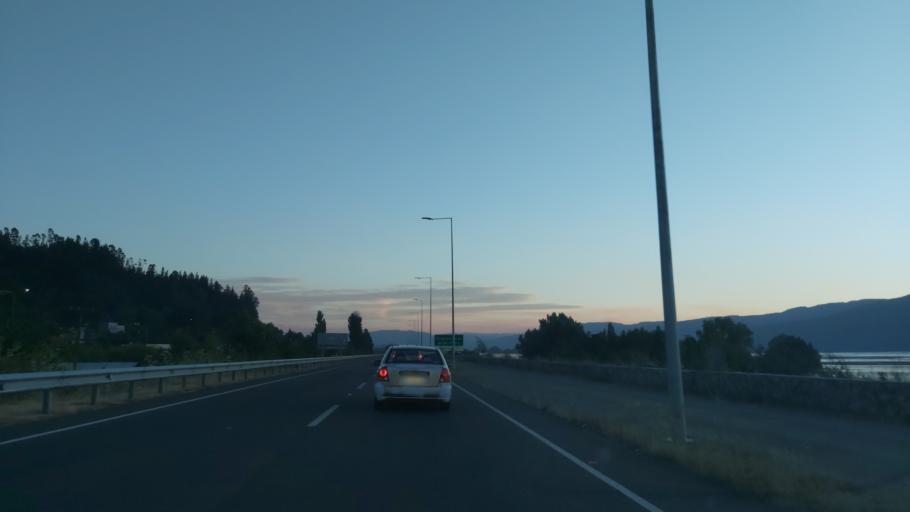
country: CL
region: Biobio
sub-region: Provincia de Concepcion
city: Chiguayante
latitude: -36.8819
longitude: -73.0387
